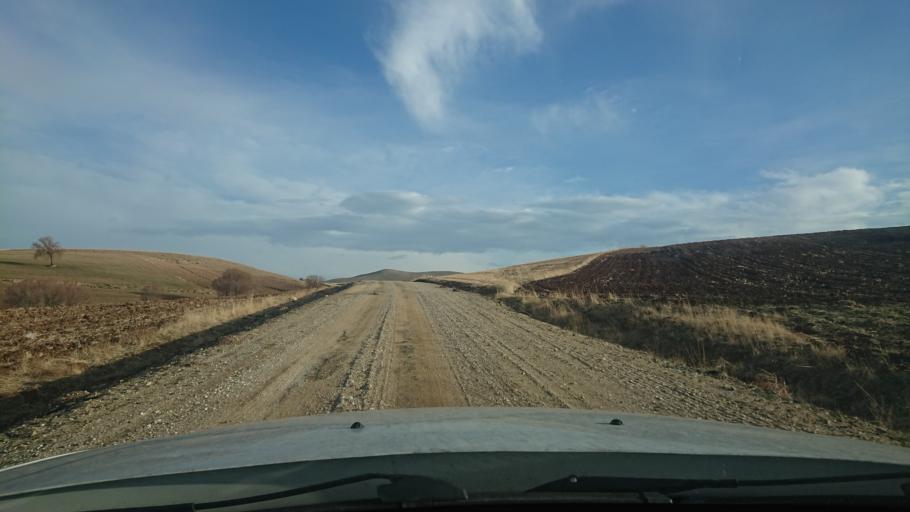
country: TR
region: Aksaray
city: Acipinar
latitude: 38.6960
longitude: 33.8721
